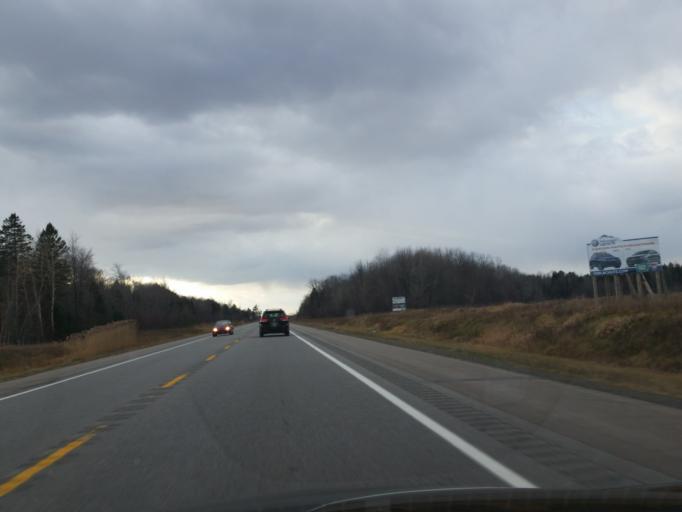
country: CA
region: Quebec
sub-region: Laurentides
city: Lachute
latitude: 45.6450
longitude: -74.2525
